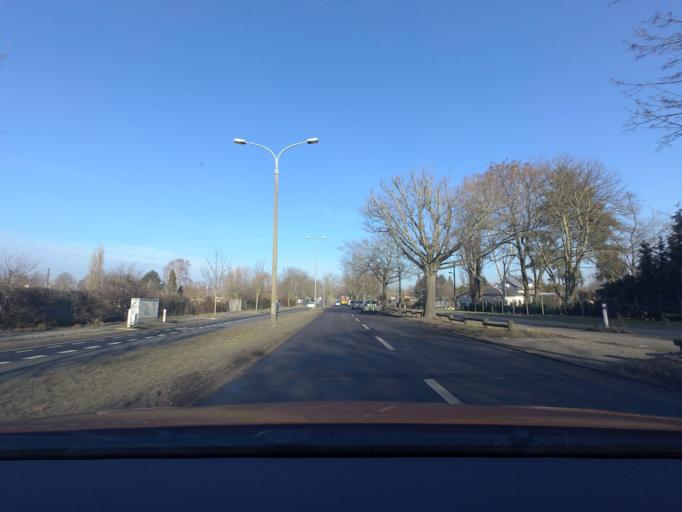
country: DE
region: Berlin
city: Niederschonhausen
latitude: 52.5996
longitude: 13.4029
